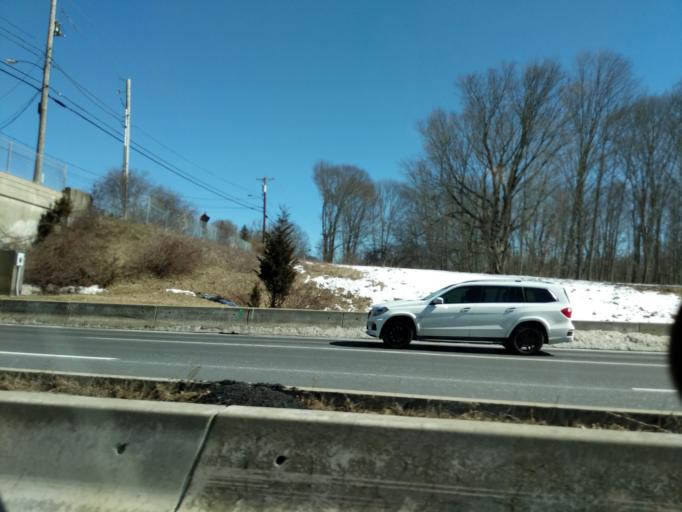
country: US
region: Rhode Island
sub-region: Providence County
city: North Providence
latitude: 41.9022
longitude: -71.4472
